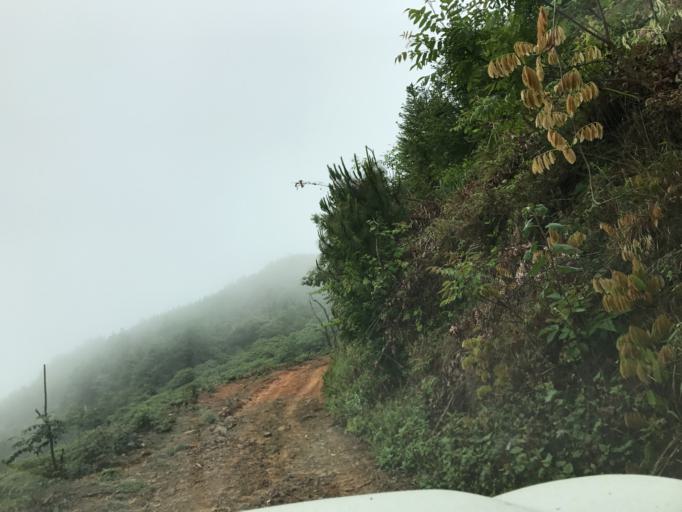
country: CN
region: Guangxi Zhuangzu Zizhiqu
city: Leli
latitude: 24.8052
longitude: 106.0800
